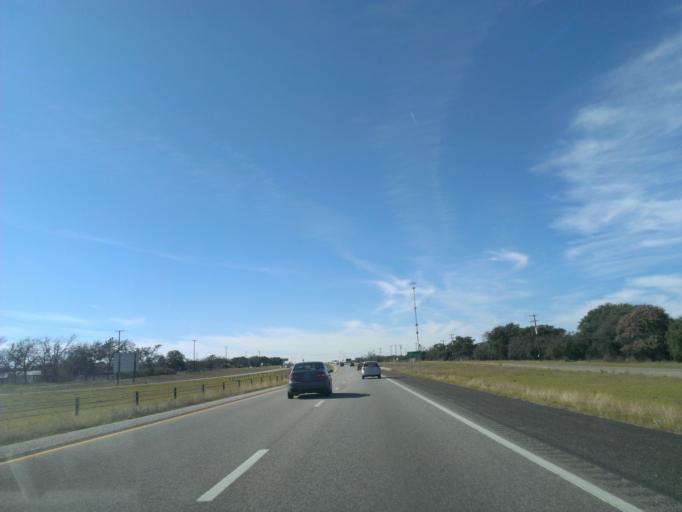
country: US
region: Texas
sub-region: Bell County
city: Belton
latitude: 31.0561
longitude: -97.5189
